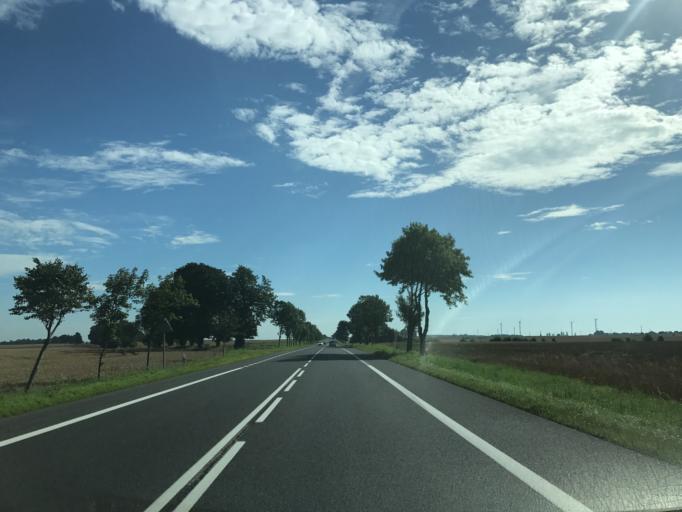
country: PL
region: West Pomeranian Voivodeship
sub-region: Powiat slawienski
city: Slawno
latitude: 54.3736
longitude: 16.7342
